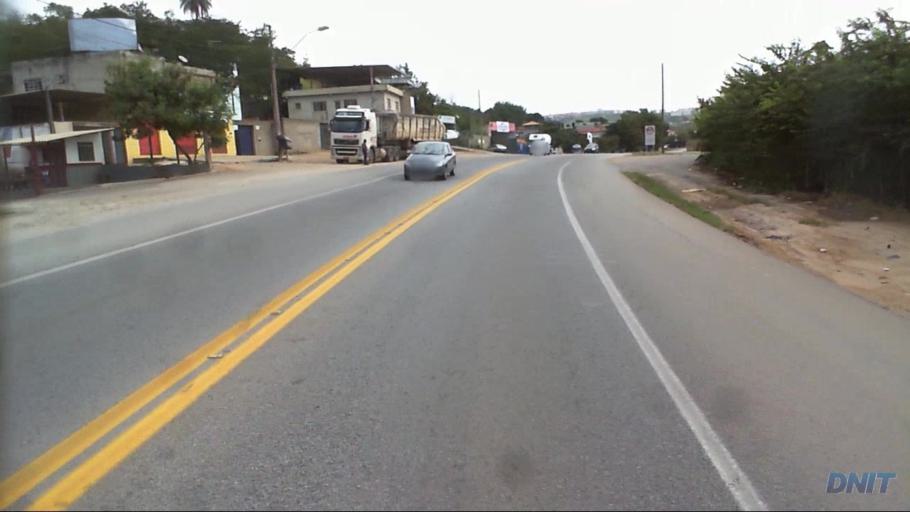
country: BR
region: Minas Gerais
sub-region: Santa Luzia
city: Santa Luzia
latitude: -19.8419
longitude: -43.8628
